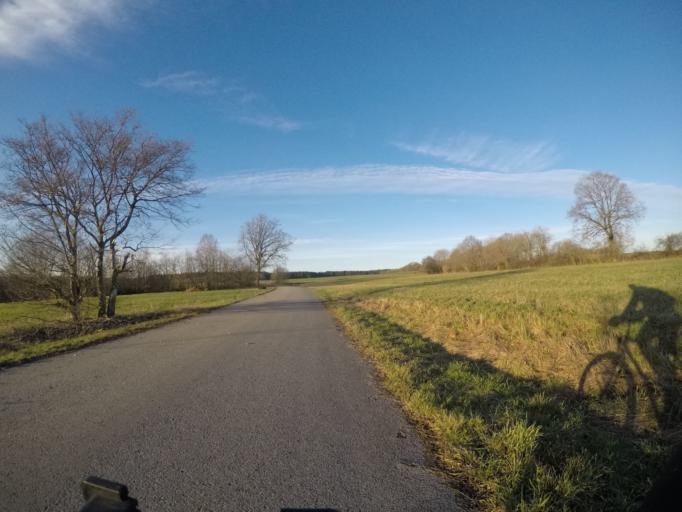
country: BE
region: Wallonia
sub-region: Province du Luxembourg
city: Habay-la-Vieille
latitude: 49.7243
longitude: 5.5936
